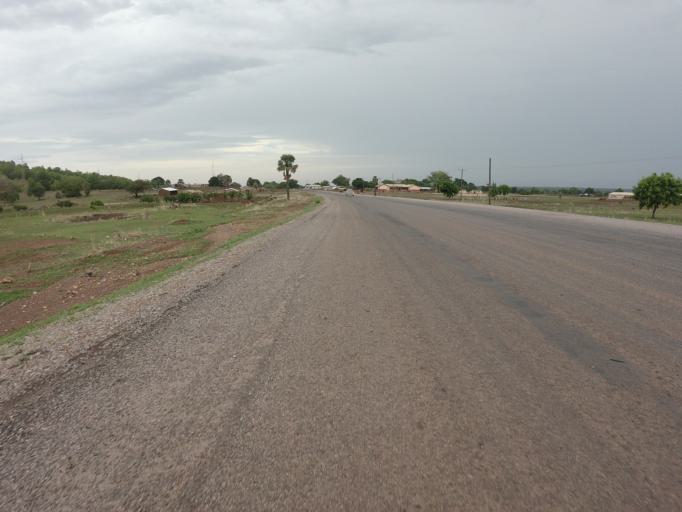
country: GH
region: Upper East
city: Bolgatanga
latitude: 10.8434
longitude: -0.6878
